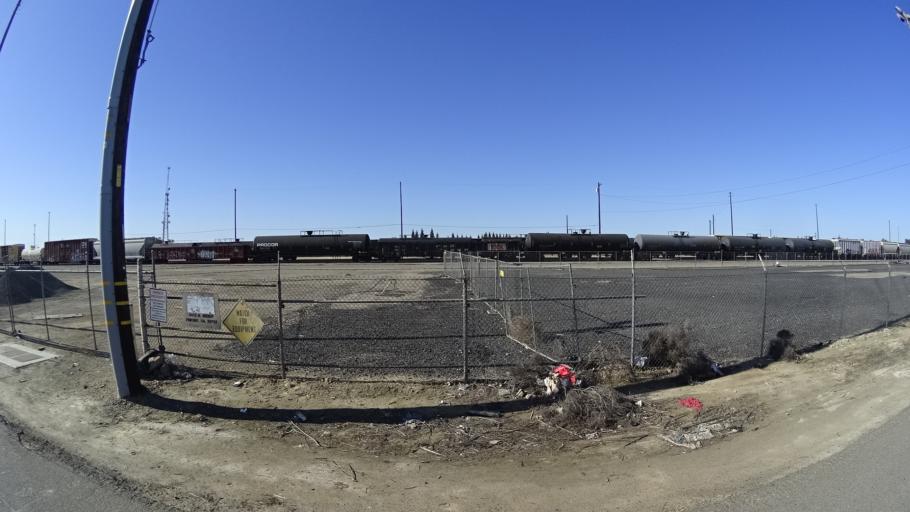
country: US
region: California
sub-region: Fresno County
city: West Park
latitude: 36.7881
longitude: -119.8523
